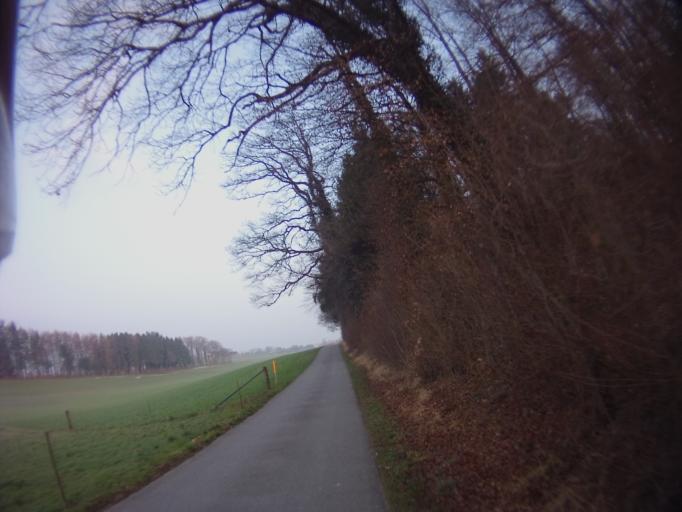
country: CH
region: Zurich
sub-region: Bezirk Affoltern
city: Knonau
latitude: 47.2296
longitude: 8.4413
